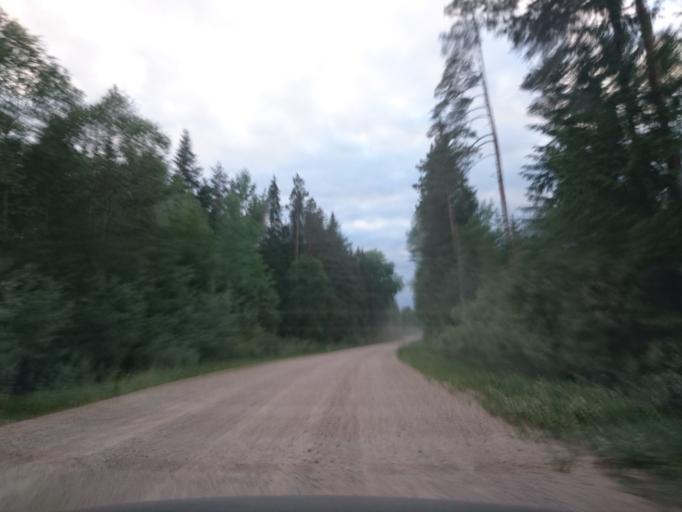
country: LV
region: Ropazu
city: Ropazi
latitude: 56.9534
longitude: 24.7265
